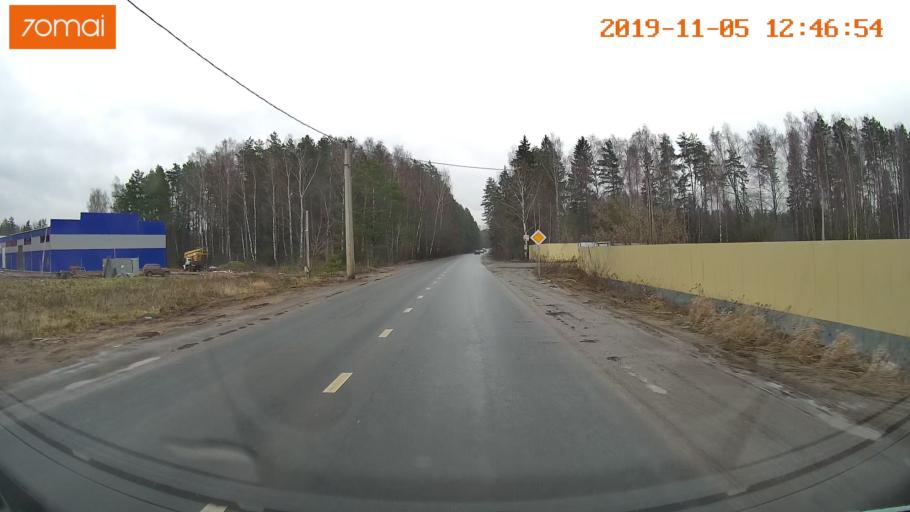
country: RU
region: Ivanovo
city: Kokhma
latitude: 56.9713
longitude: 41.0809
